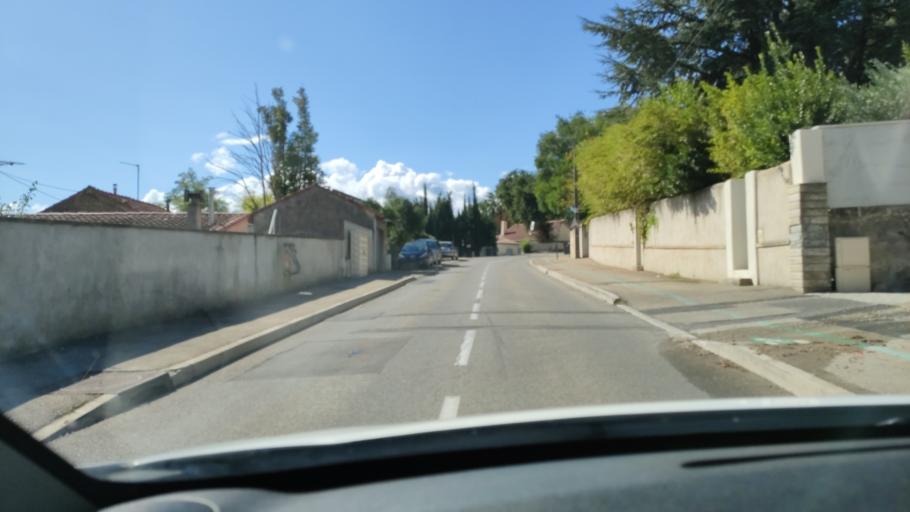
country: FR
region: Languedoc-Roussillon
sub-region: Departement du Gard
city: Villeneuve-les-Avignon
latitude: 43.9694
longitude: 4.7918
